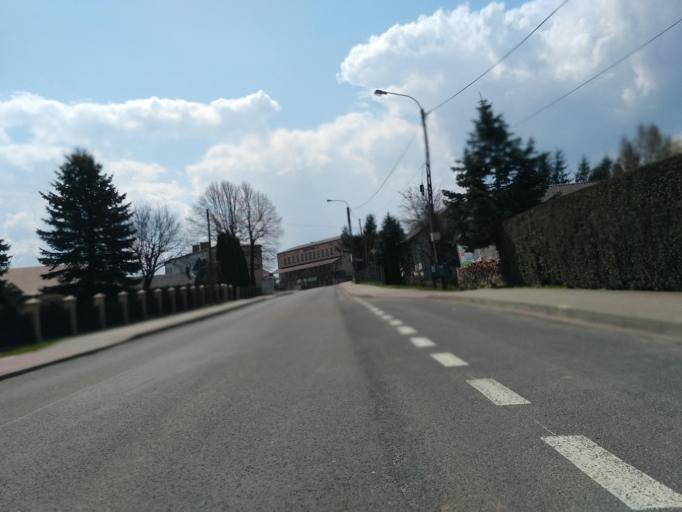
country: PL
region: Subcarpathian Voivodeship
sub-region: Powiat sanocki
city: Bukowsko
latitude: 49.5099
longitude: 22.0307
